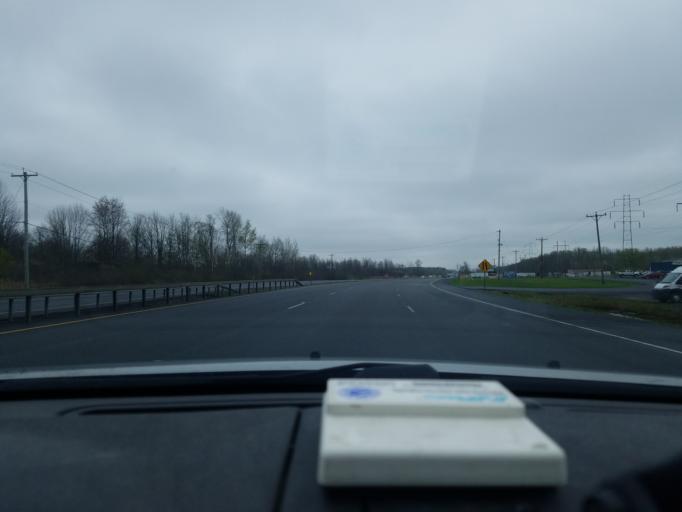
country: US
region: New York
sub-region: Onondaga County
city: North Syracuse
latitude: 43.1267
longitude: -76.0790
